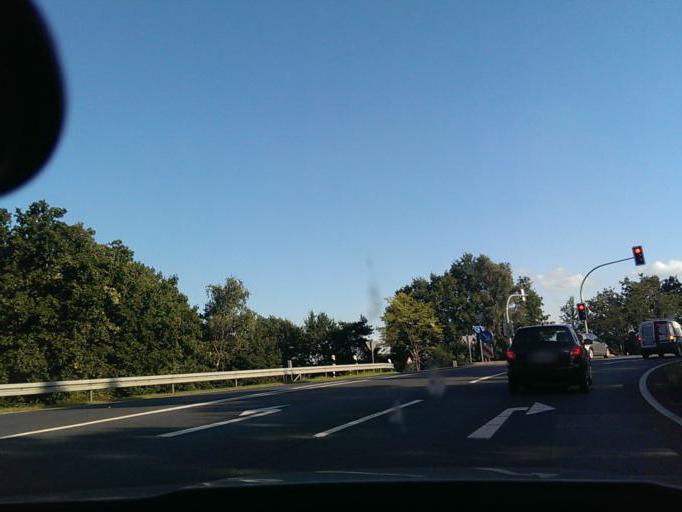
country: DE
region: Lower Saxony
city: Elze
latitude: 52.5575
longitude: 9.7929
